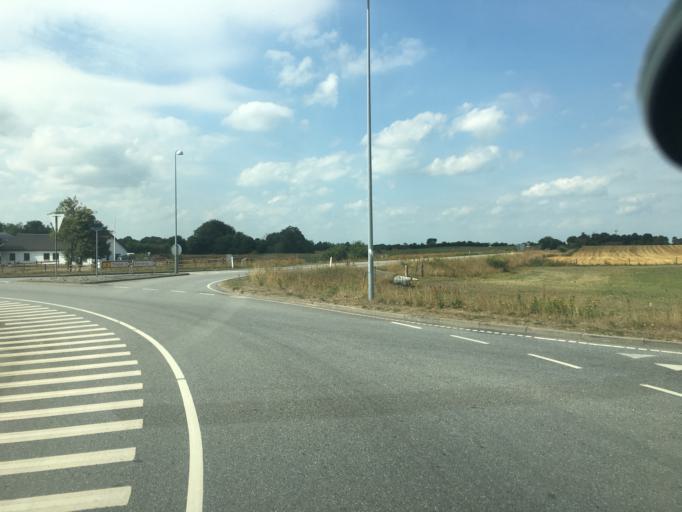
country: DK
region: South Denmark
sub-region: Aabenraa Kommune
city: Krusa
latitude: 54.9397
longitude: 9.3624
